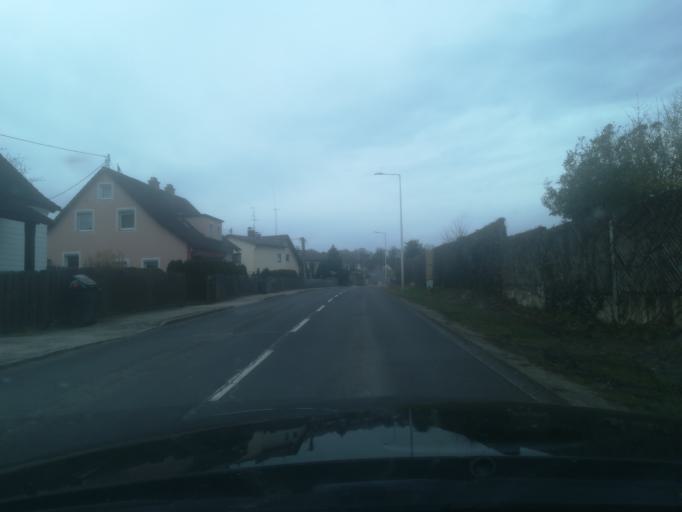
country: AT
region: Upper Austria
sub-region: Wels-Land
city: Lambach
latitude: 48.0933
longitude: 13.9002
